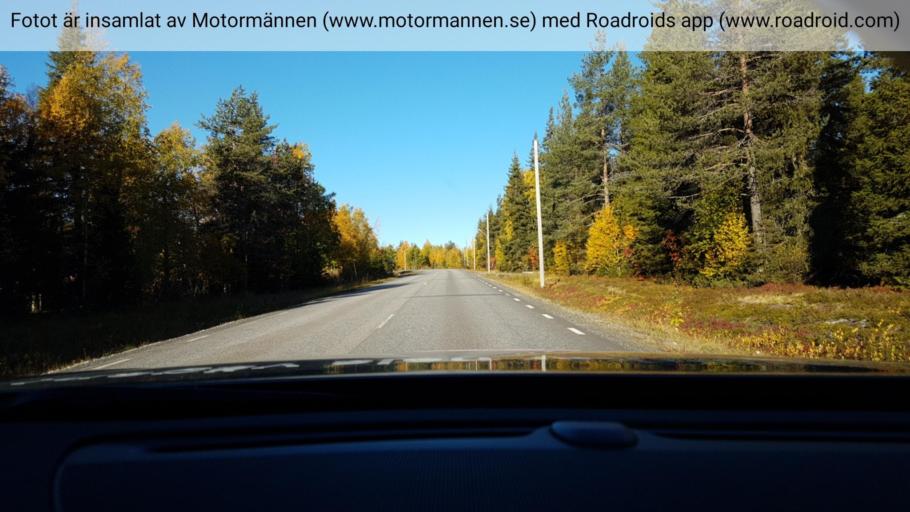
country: SE
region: Vaesterbotten
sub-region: Skelleftea Kommun
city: Storvik
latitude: 65.3604
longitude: 20.4434
